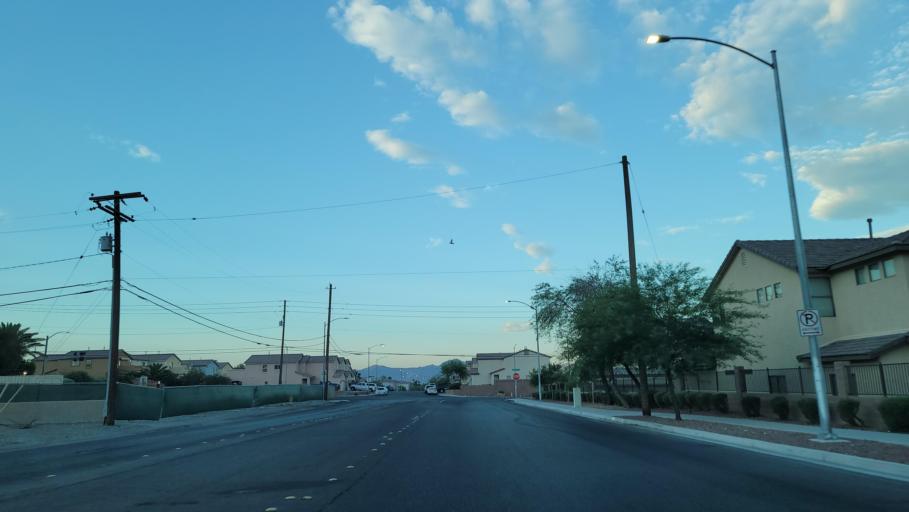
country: US
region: Nevada
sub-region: Clark County
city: Sunrise Manor
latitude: 36.1605
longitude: -115.0355
